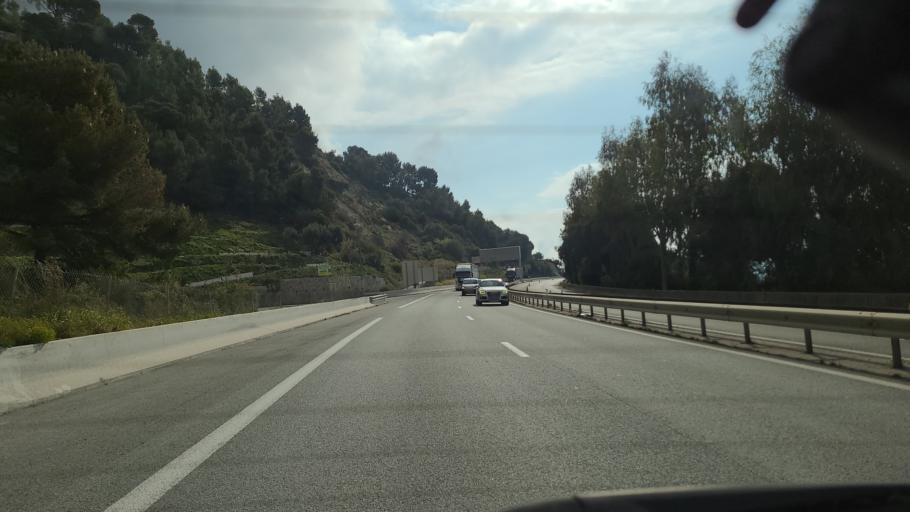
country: FR
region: Provence-Alpes-Cote d'Azur
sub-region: Departement des Alpes-Maritimes
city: Menton
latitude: 43.7931
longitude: 7.5100
